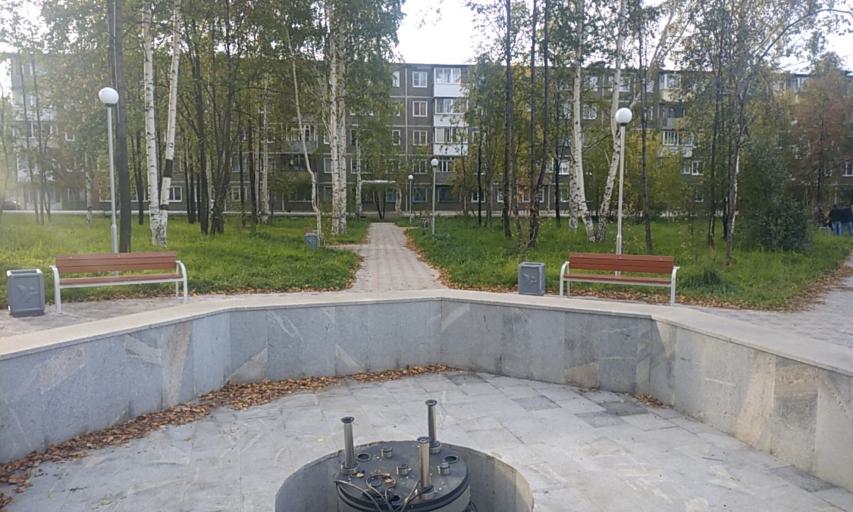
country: RU
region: Sverdlovsk
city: Krasnoural'sk
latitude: 58.3566
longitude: 60.0428
